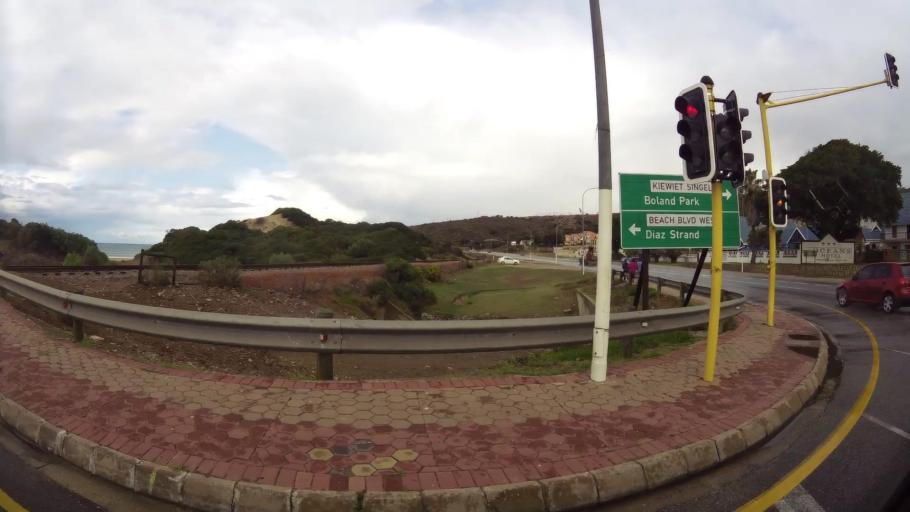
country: ZA
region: Western Cape
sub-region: Eden District Municipality
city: Mossel Bay
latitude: -34.1635
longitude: 22.1087
